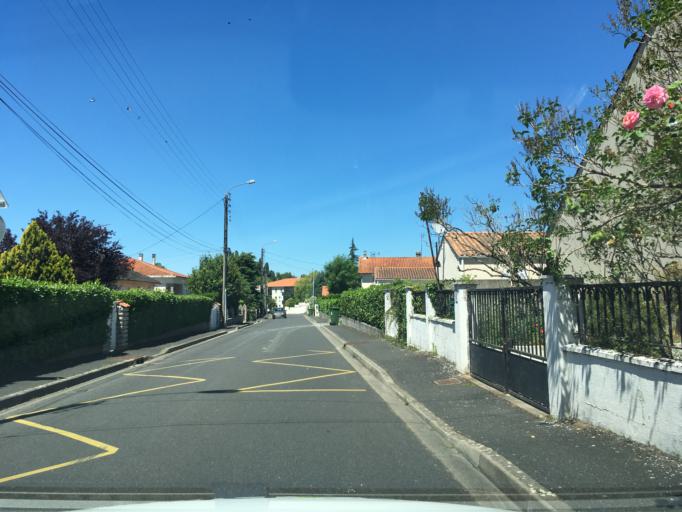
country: FR
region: Poitou-Charentes
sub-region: Departement des Deux-Sevres
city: Niort
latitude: 46.3303
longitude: -0.4268
